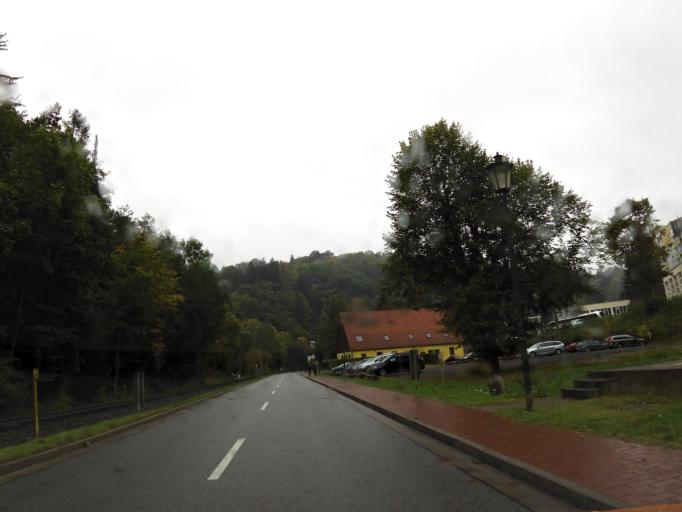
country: DE
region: Saxony-Anhalt
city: Harzgerode
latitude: 51.6517
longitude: 11.1171
